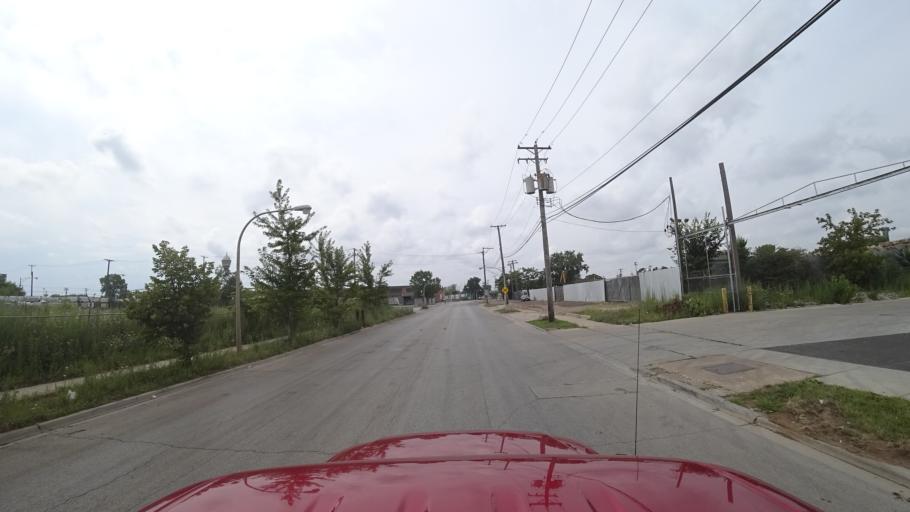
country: US
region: Illinois
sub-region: Cook County
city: Chicago
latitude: 41.8259
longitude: -87.6556
